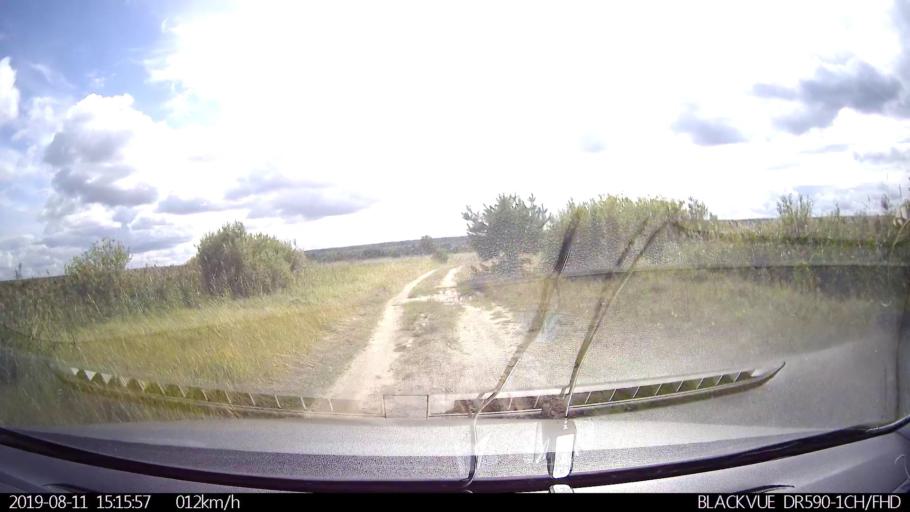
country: RU
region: Ulyanovsk
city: Ignatovka
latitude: 53.8482
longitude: 47.5890
